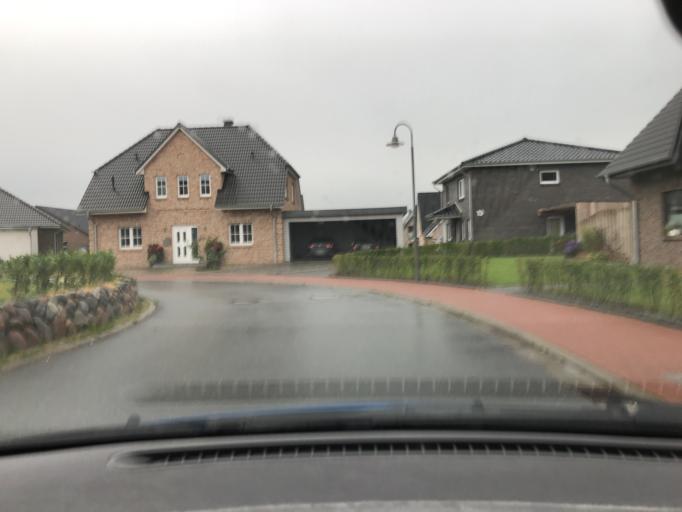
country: DE
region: Schleswig-Holstein
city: Fahrdorf
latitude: 54.5031
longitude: 9.6144
